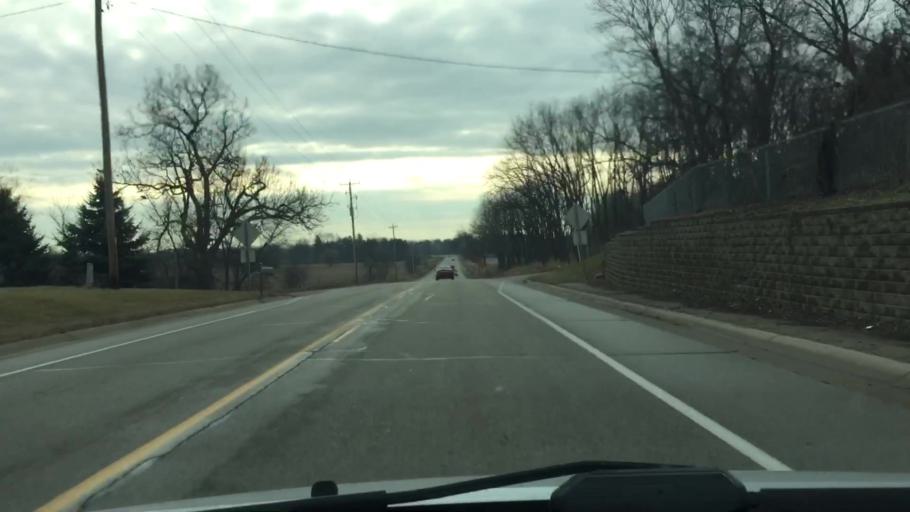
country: US
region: Wisconsin
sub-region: Jefferson County
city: Palmyra
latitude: 42.7968
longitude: -88.5630
